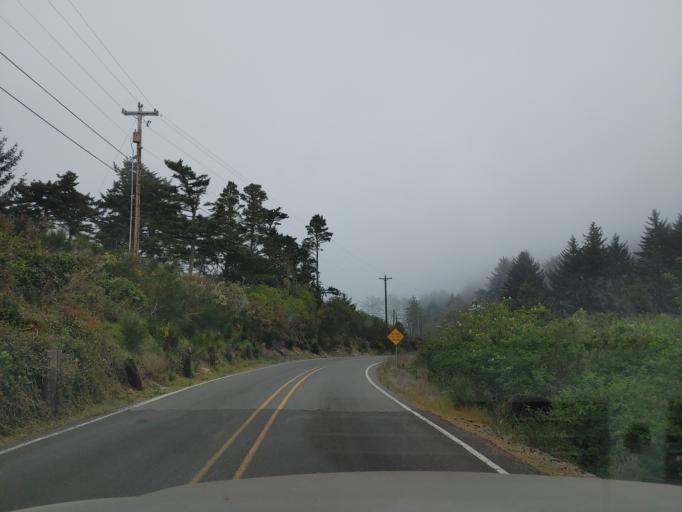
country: US
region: Oregon
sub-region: Coos County
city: Lakeside
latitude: 43.6651
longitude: -124.1974
